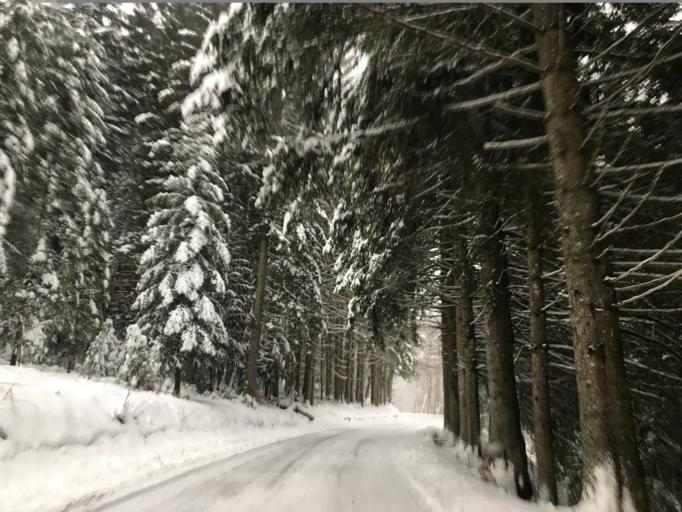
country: FR
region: Auvergne
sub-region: Departement du Puy-de-Dome
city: Job
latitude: 45.7209
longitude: 3.6975
